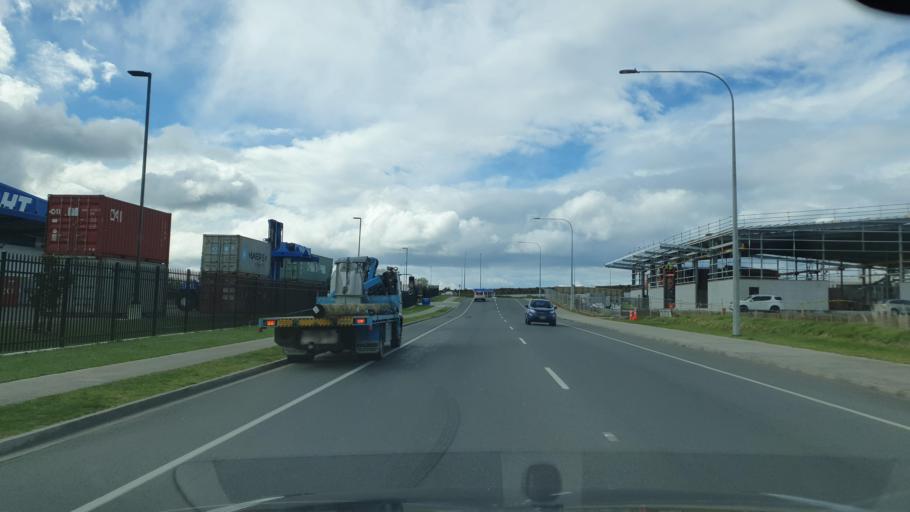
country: NZ
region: Bay of Plenty
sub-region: Tauranga City
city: Tauranga
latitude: -37.6924
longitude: 176.2402
